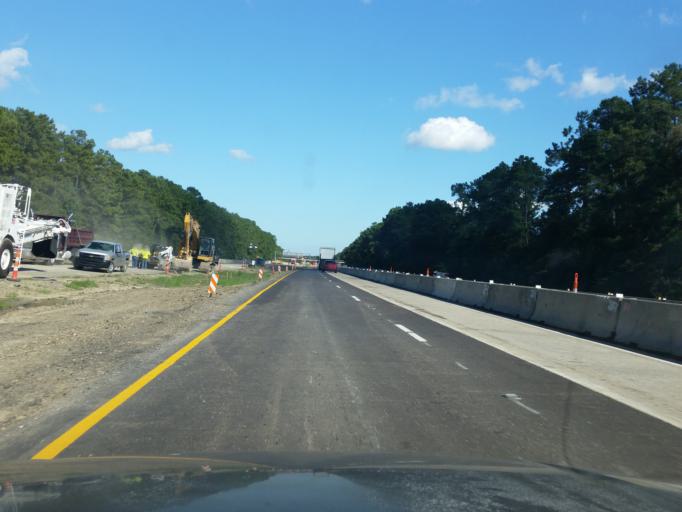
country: US
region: Louisiana
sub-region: Saint Tammany Parish
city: Slidell
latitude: 30.3033
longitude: -89.7312
